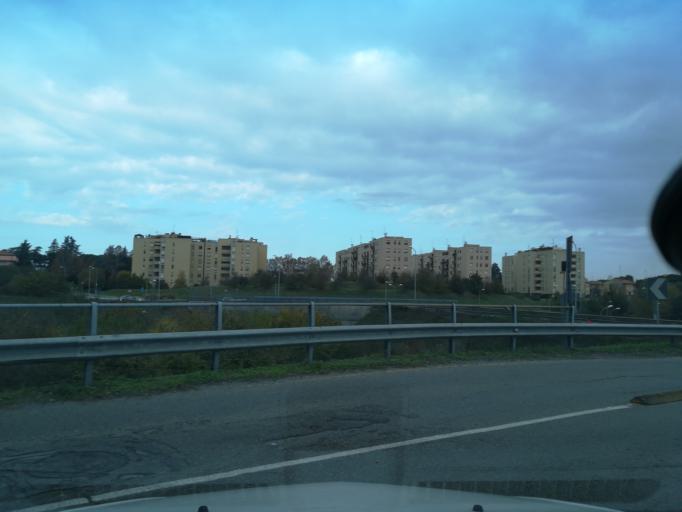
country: IT
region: Emilia-Romagna
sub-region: Provincia di Bologna
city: Imola
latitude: 44.3633
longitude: 11.6985
